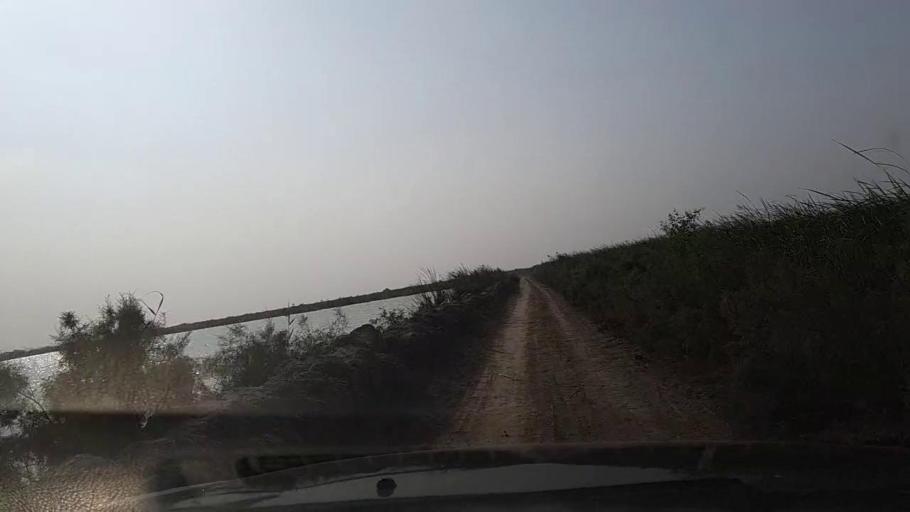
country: PK
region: Sindh
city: Mirpur Batoro
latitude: 24.6476
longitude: 68.2843
